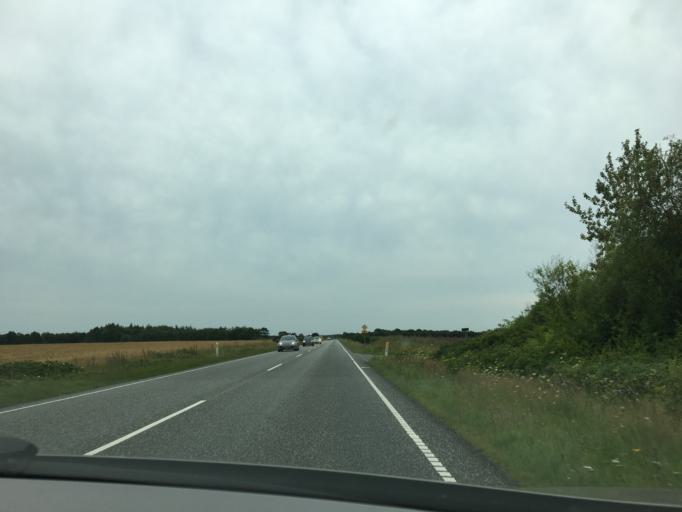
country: DK
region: Central Jutland
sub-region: Herning Kommune
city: Sunds
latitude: 56.2319
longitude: 9.0085
